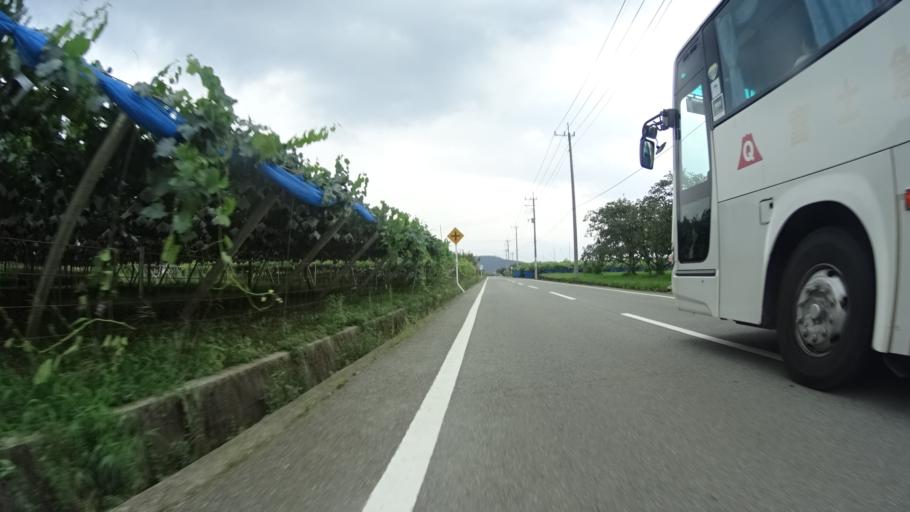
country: JP
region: Yamanashi
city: Enzan
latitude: 35.7330
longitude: 138.7223
